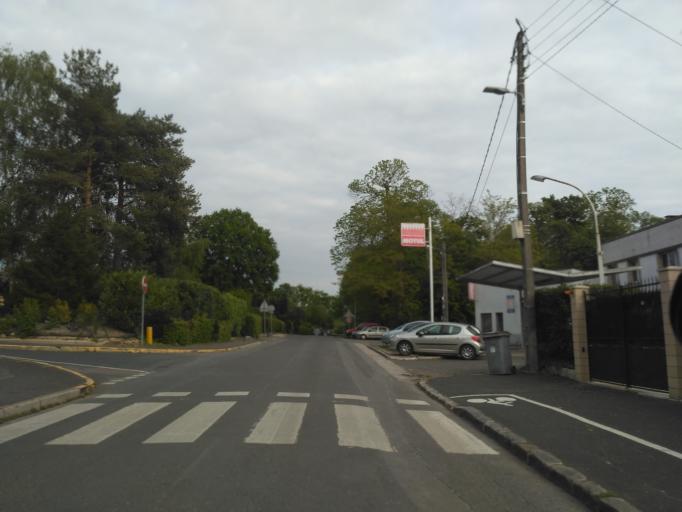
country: FR
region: Ile-de-France
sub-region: Departement de Seine-et-Marne
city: Cesson
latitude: 48.5619
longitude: 2.6104
